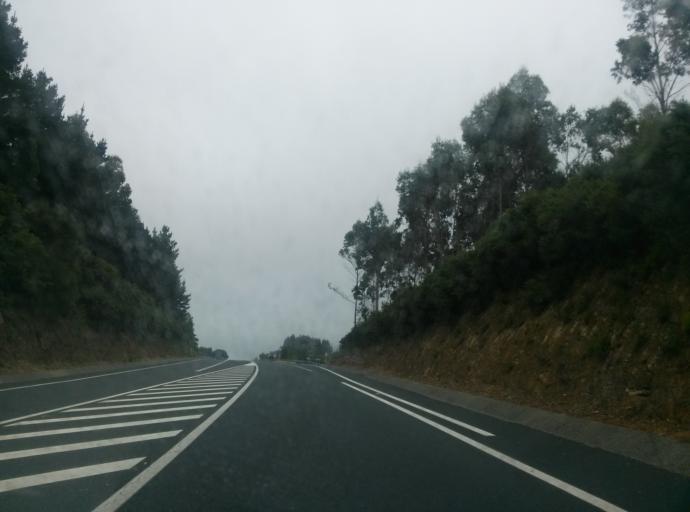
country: ES
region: Galicia
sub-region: Provincia de Lugo
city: Muras
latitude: 43.4342
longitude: -7.7390
